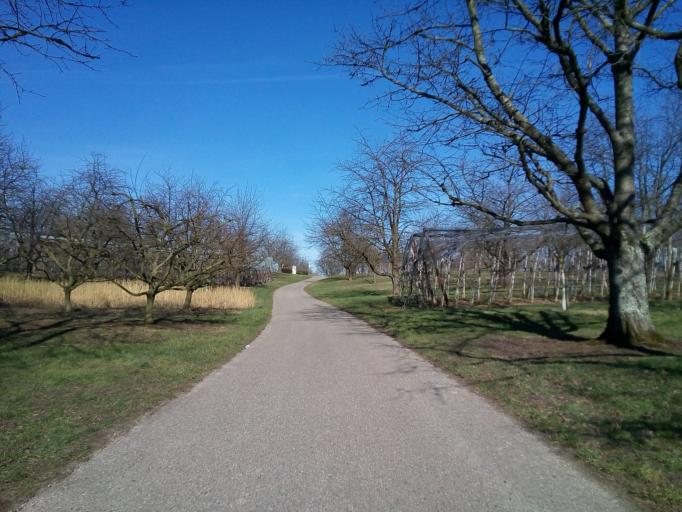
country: DE
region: Baden-Wuerttemberg
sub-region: Freiburg Region
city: Achern
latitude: 48.6082
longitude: 8.0605
